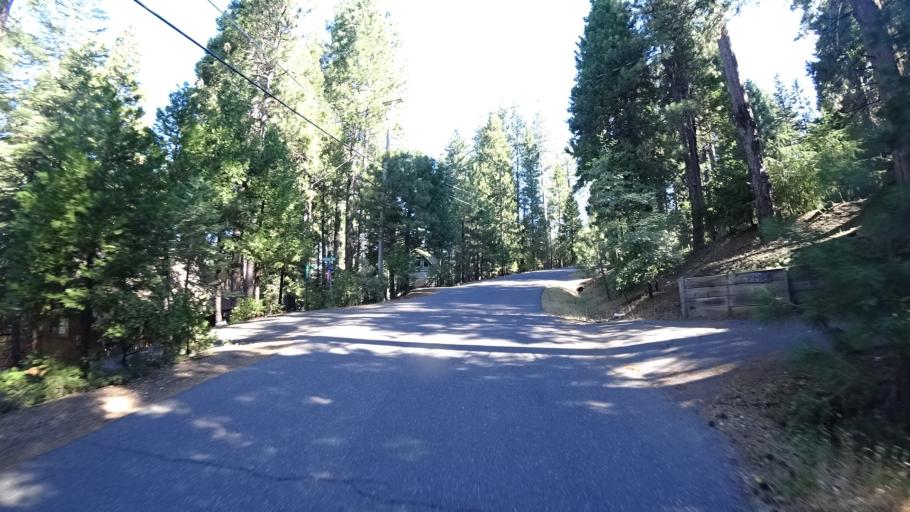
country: US
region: California
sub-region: Calaveras County
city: Arnold
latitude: 38.2511
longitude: -120.3239
